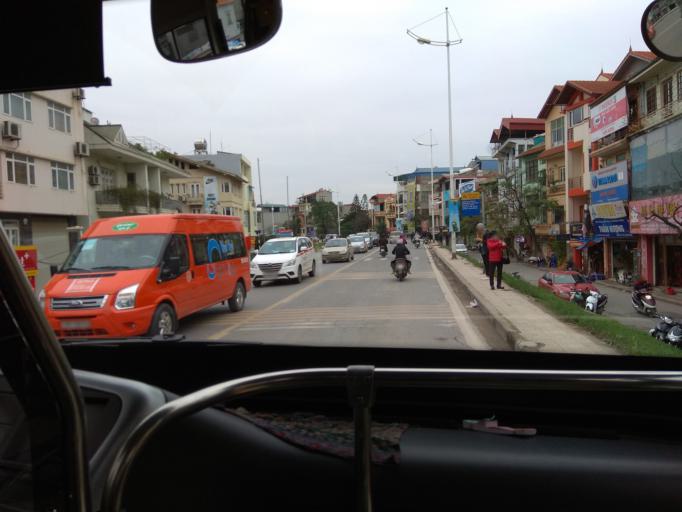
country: VN
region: Ha Noi
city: Tay Ho
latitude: 21.0634
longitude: 105.8320
